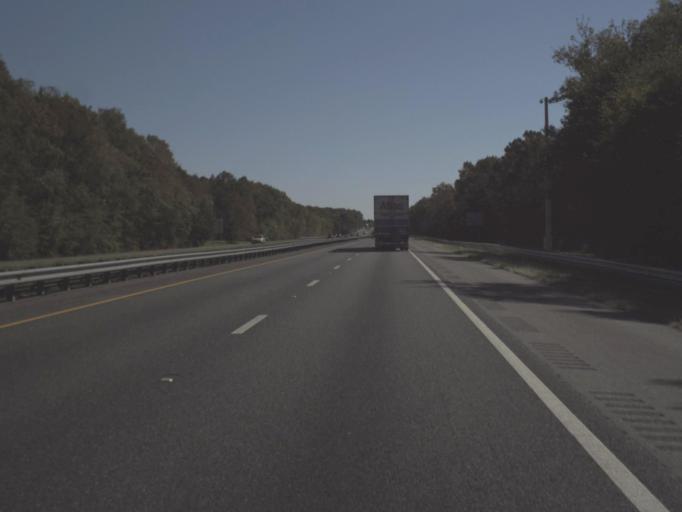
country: US
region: Florida
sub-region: Sumter County
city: Wildwood
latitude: 28.8430
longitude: -82.0630
